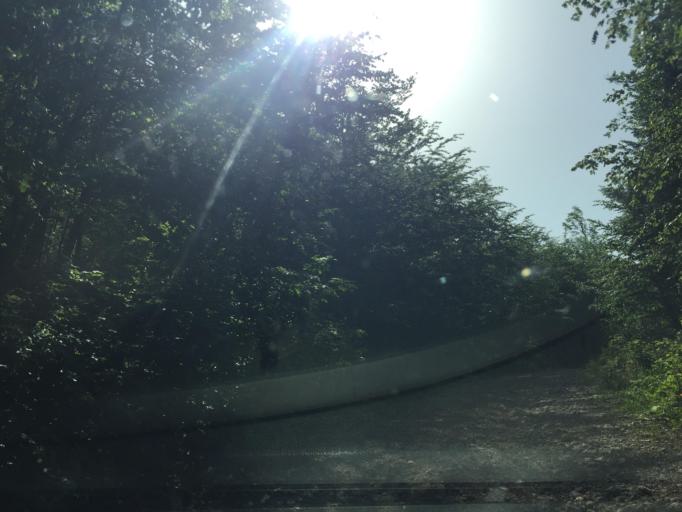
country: HR
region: Primorsko-Goranska
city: Podhum
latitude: 45.4171
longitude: 14.5816
